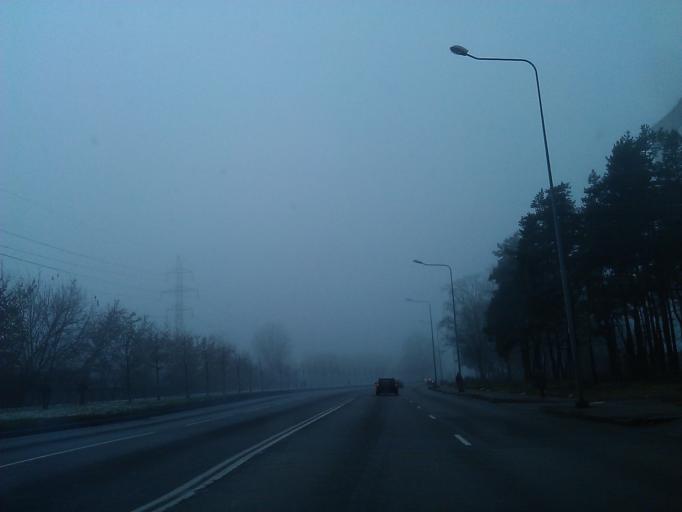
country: LV
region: Stopini
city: Ulbroka
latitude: 56.9328
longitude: 24.2153
